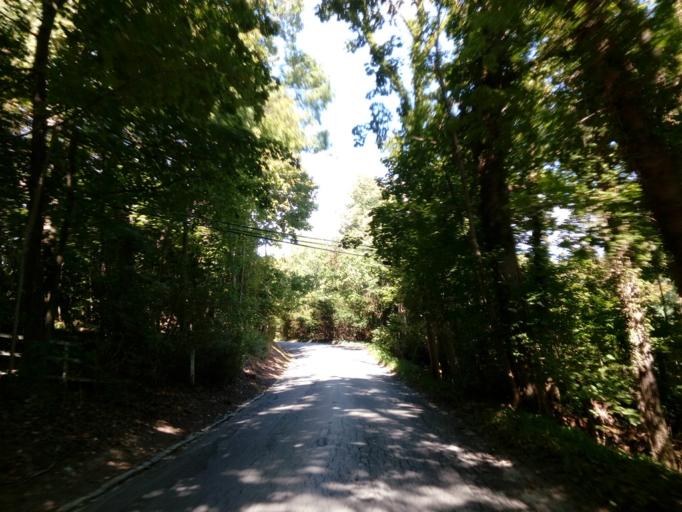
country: US
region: New York
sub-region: Nassau County
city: Laurel Hollow
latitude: 40.8621
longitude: -73.4748
